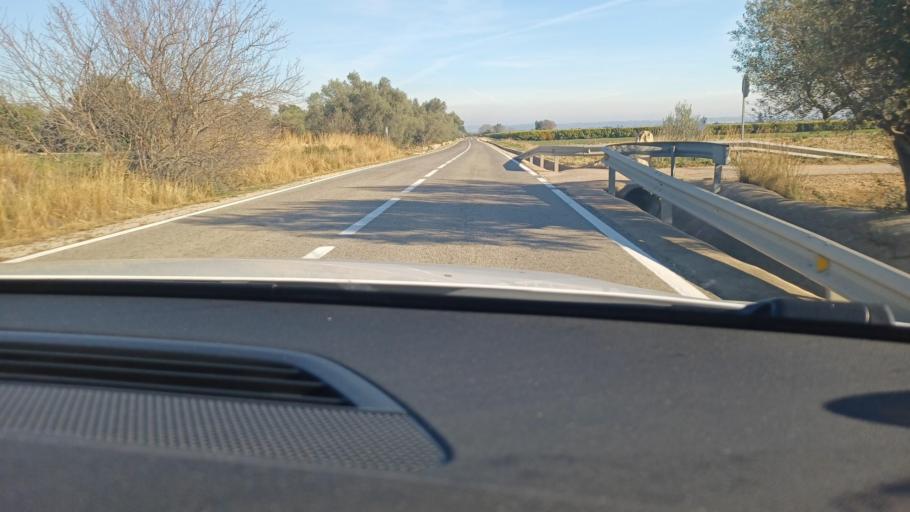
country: ES
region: Catalonia
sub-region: Provincia de Tarragona
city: Santa Barbara
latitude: 40.7207
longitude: 0.4308
